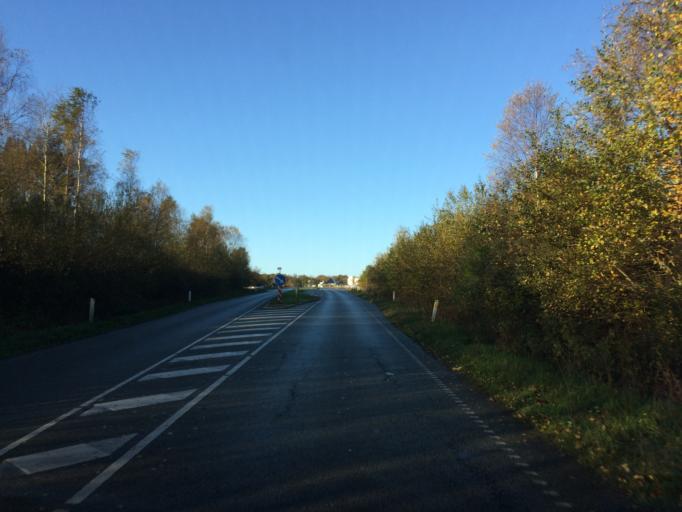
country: DK
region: South Denmark
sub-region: Kolding Kommune
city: Kolding
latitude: 55.5125
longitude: 9.5126
